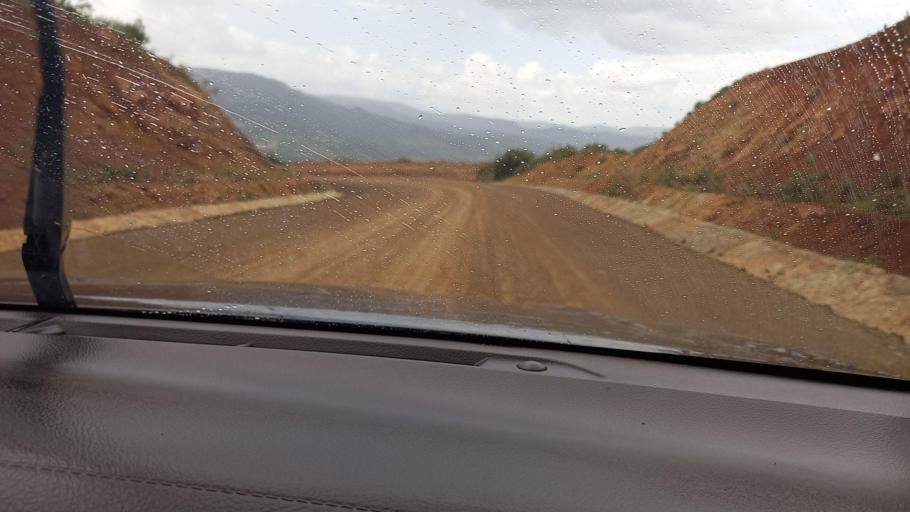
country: ET
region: Southern Nations, Nationalities, and People's Region
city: Mizan Teferi
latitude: 6.1812
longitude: 35.7002
